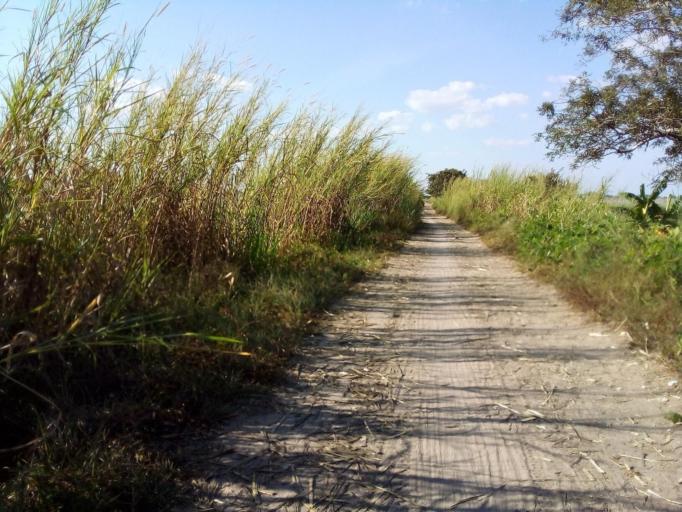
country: MZ
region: Zambezia
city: Quelimane
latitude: -17.5839
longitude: 36.8432
